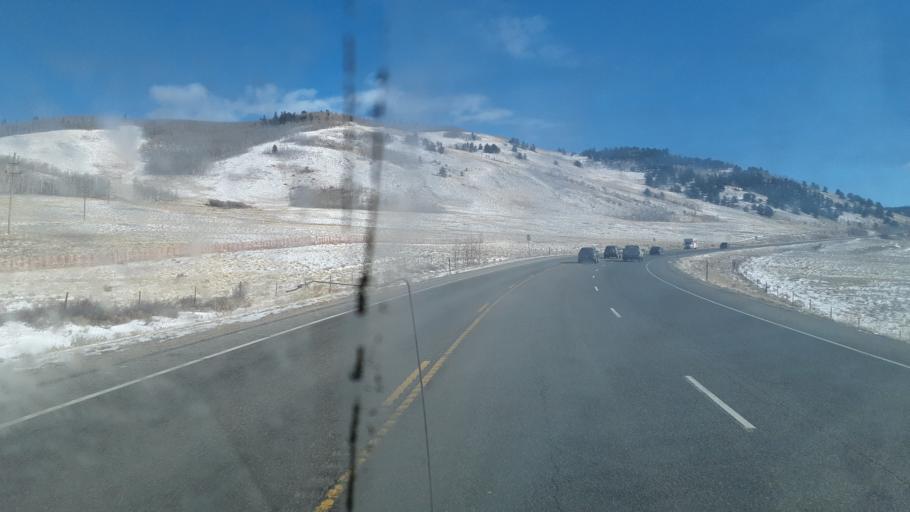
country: US
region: Colorado
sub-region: Summit County
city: Breckenridge
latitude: 39.4068
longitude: -105.7742
